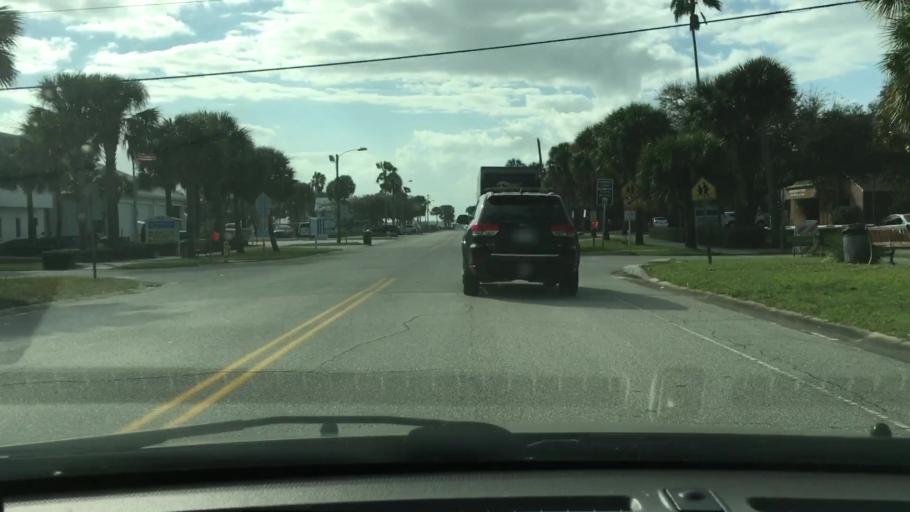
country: US
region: Florida
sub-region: Brevard County
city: Melbourne Beach
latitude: 28.0684
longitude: -80.5629
